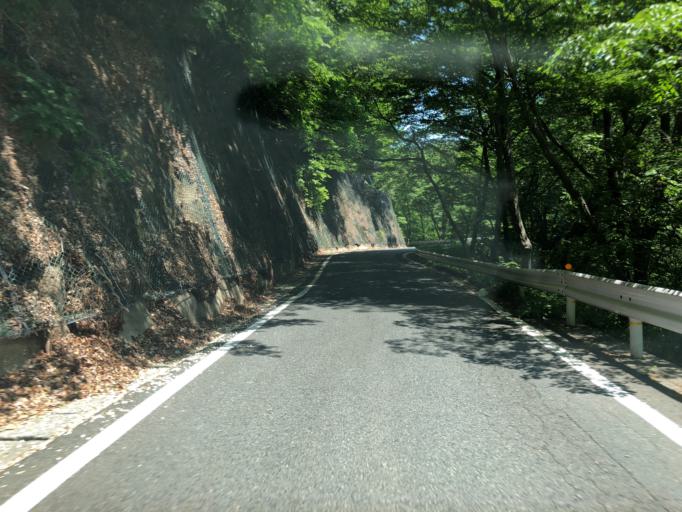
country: JP
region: Fukushima
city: Namie
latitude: 37.5137
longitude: 140.8453
